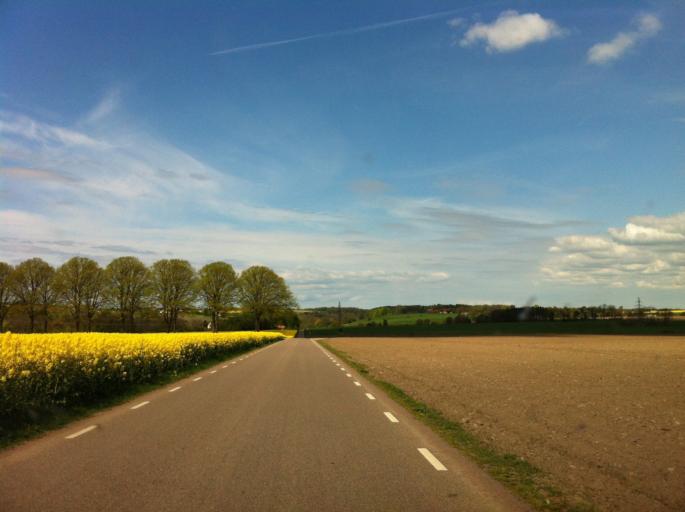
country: SE
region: Skane
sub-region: Landskrona
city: Asmundtorp
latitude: 55.9405
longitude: 12.9322
